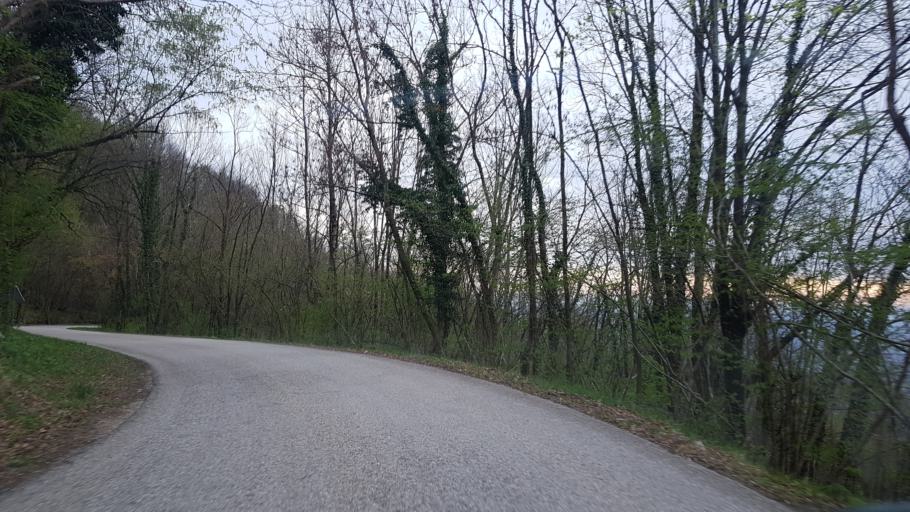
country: SI
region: Kanal
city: Deskle
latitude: 46.0369
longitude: 13.5663
